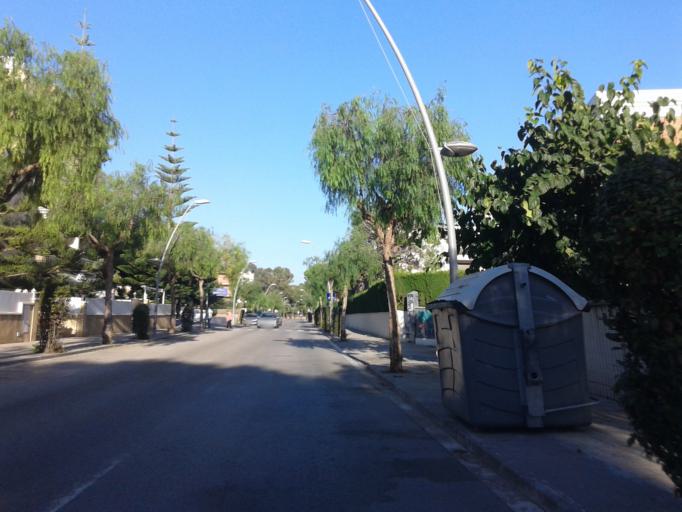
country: ES
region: Catalonia
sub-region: Provincia de Tarragona
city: El Vendrell
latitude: 41.1816
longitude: 1.5270
